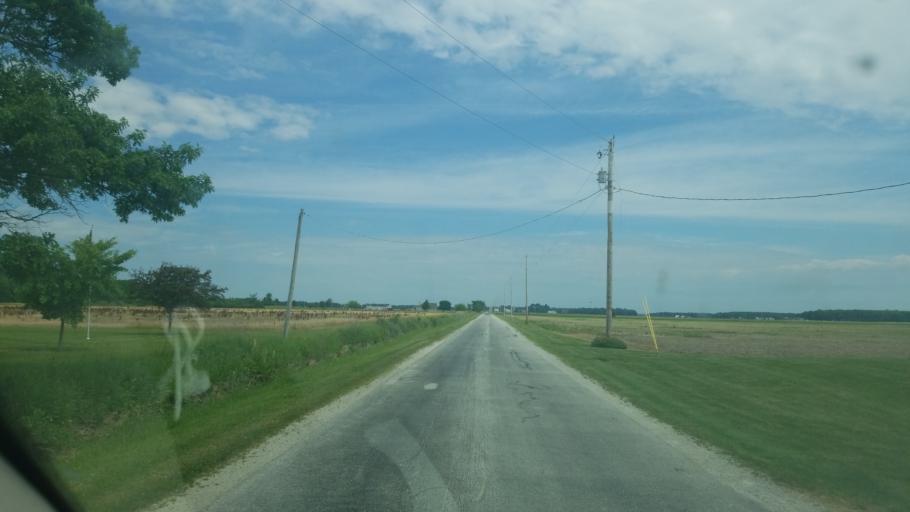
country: US
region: Ohio
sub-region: Wood County
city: North Baltimore
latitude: 41.2213
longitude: -83.5732
